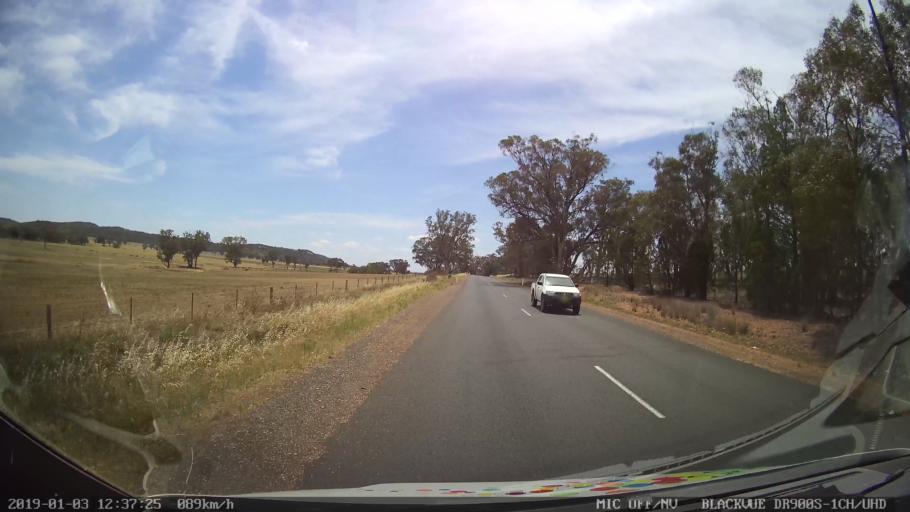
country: AU
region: New South Wales
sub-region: Weddin
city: Grenfell
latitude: -33.8429
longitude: 148.1841
